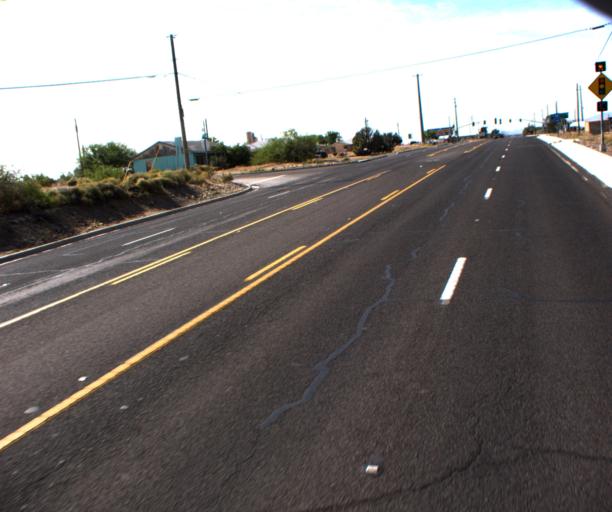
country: US
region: Arizona
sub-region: Graham County
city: Safford
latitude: 32.8044
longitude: -109.7078
